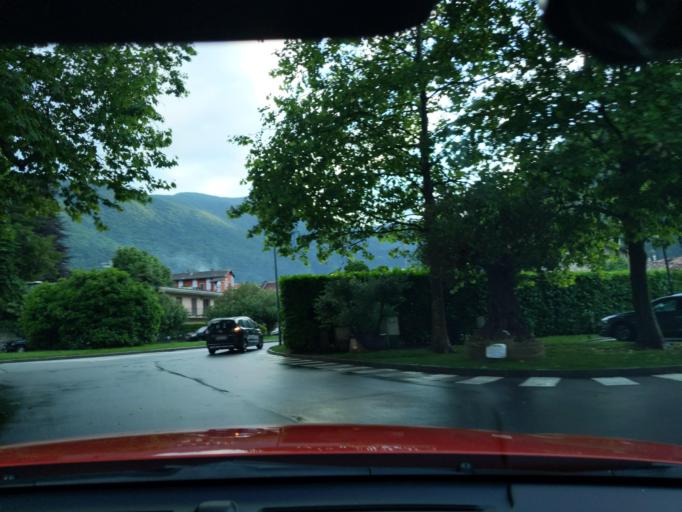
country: IT
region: Piedmont
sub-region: Provincia Verbano-Cusio-Ossola
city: Cannobio
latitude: 46.0672
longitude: 8.6992
